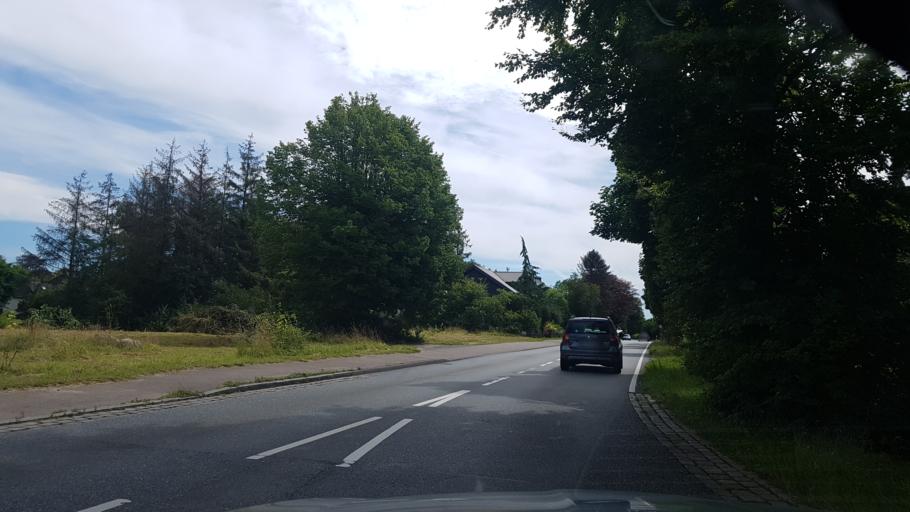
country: DE
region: Schleswig-Holstein
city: Gross Buchwald
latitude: 54.1635
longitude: 10.0794
